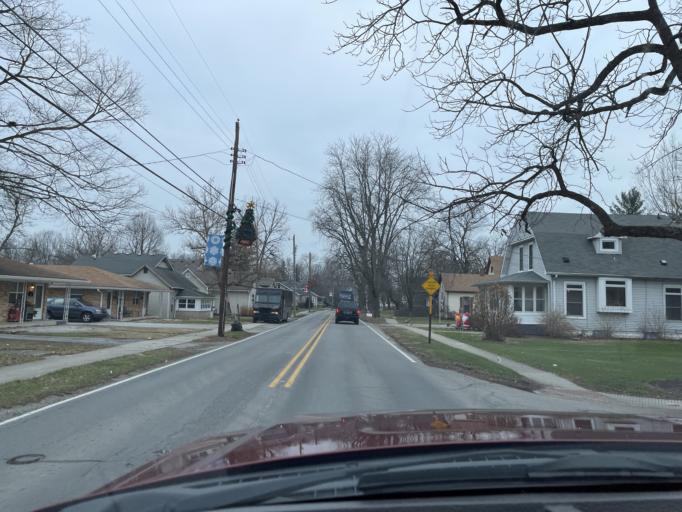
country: US
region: Indiana
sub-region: Hendricks County
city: Brownsburg
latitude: 39.8388
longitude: -86.4003
